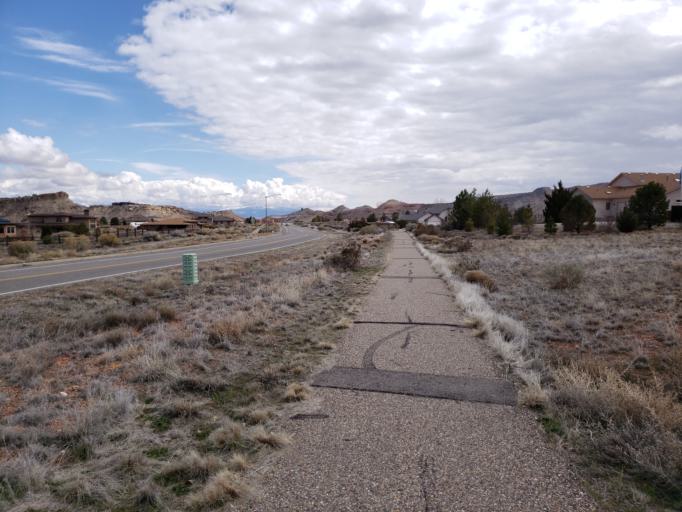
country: US
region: Colorado
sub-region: Mesa County
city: Redlands
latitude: 39.0538
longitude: -108.6427
